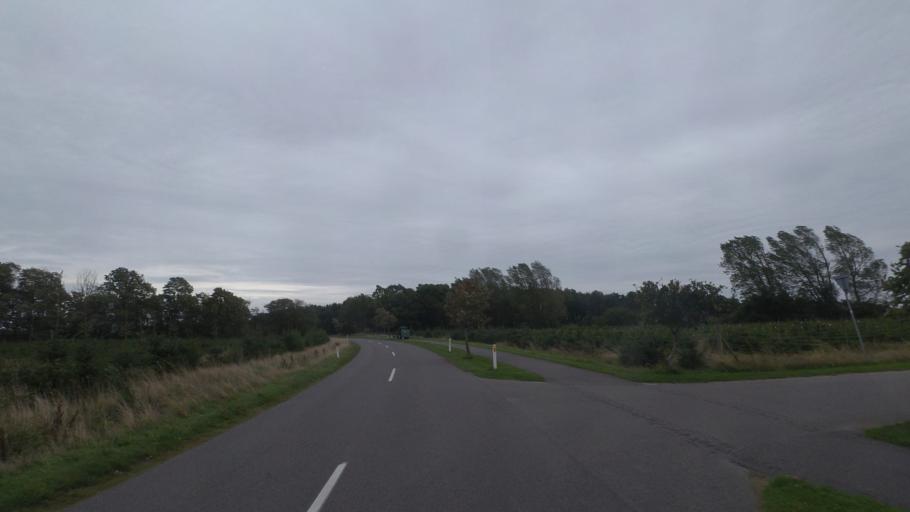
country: DK
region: Capital Region
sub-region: Bornholm Kommune
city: Akirkeby
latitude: 55.0023
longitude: 15.0003
